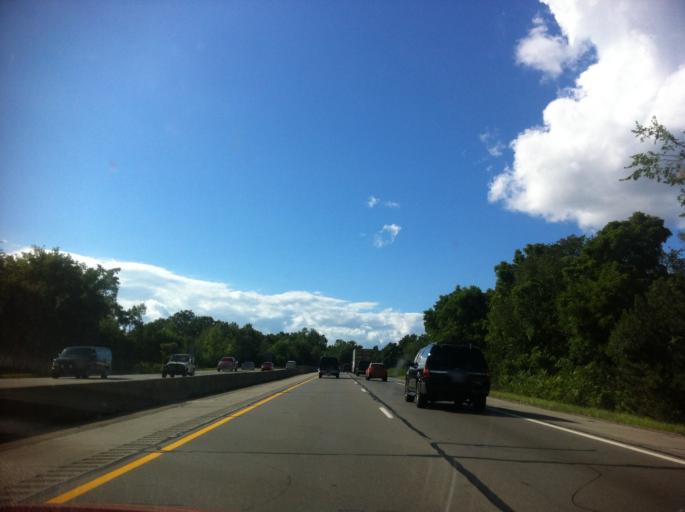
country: US
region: Michigan
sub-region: Washtenaw County
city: Ann Arbor
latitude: 42.2486
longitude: -83.7673
